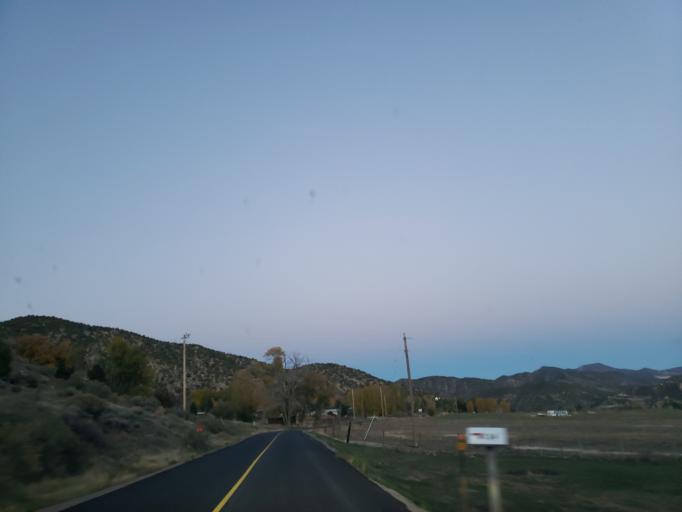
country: US
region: Colorado
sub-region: Garfield County
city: New Castle
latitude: 39.5601
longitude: -107.5749
